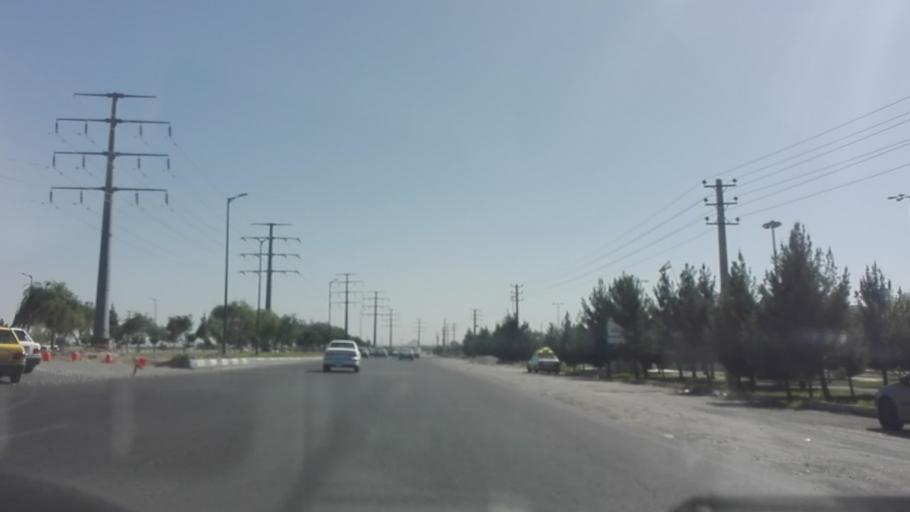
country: IR
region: Tehran
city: Shahre Jadide Andisheh
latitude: 35.6676
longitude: 51.0212
